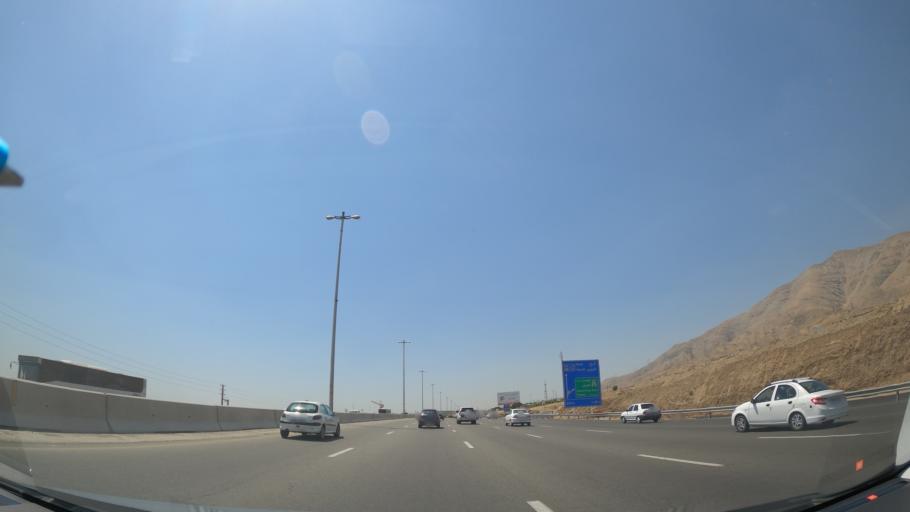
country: IR
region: Tehran
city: Shahr-e Qods
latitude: 35.7479
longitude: 51.0849
